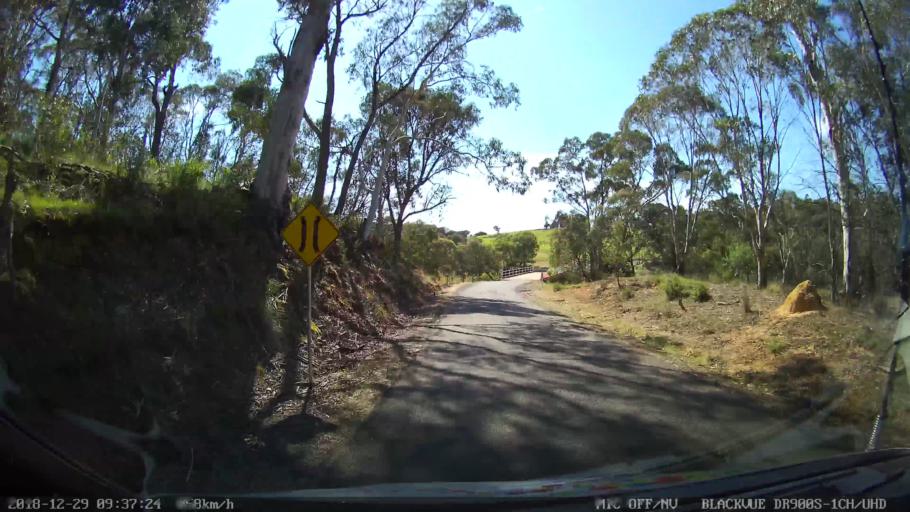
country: AU
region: New South Wales
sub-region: Upper Lachlan Shire
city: Crookwell
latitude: -34.6388
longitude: 149.3740
